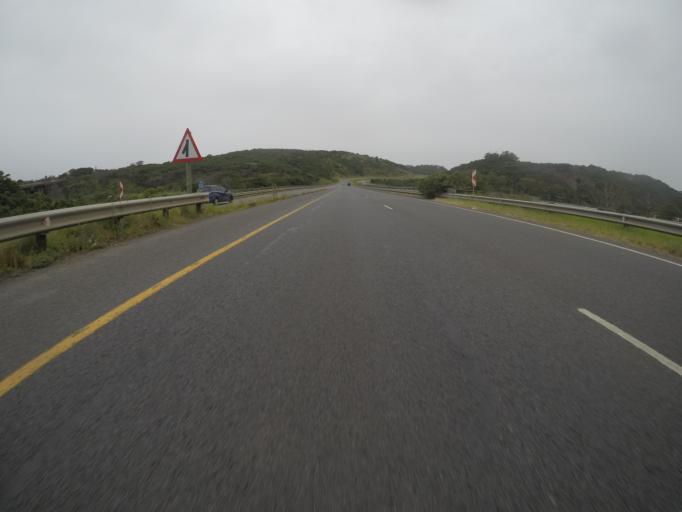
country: ZA
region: Eastern Cape
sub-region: Buffalo City Metropolitan Municipality
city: East London
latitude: -32.9649
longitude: 27.9190
